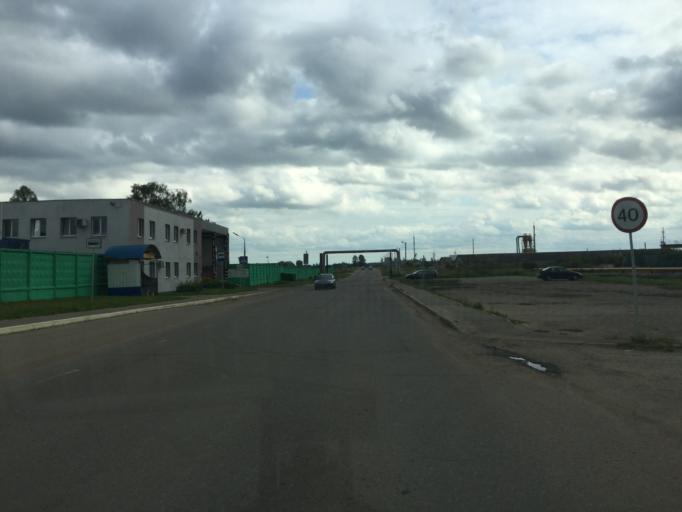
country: BY
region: Vitebsk
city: Vitebsk
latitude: 55.1597
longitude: 30.2629
